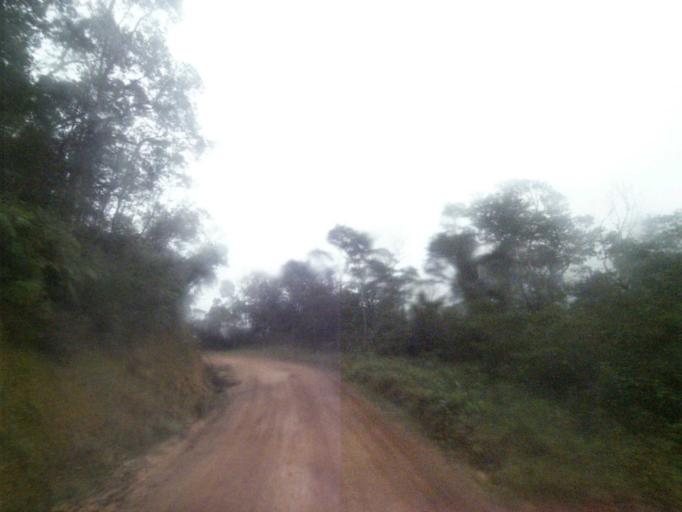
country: BR
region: Santa Catarina
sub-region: Anitapolis
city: Anitapolis
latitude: -27.8539
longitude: -49.1350
